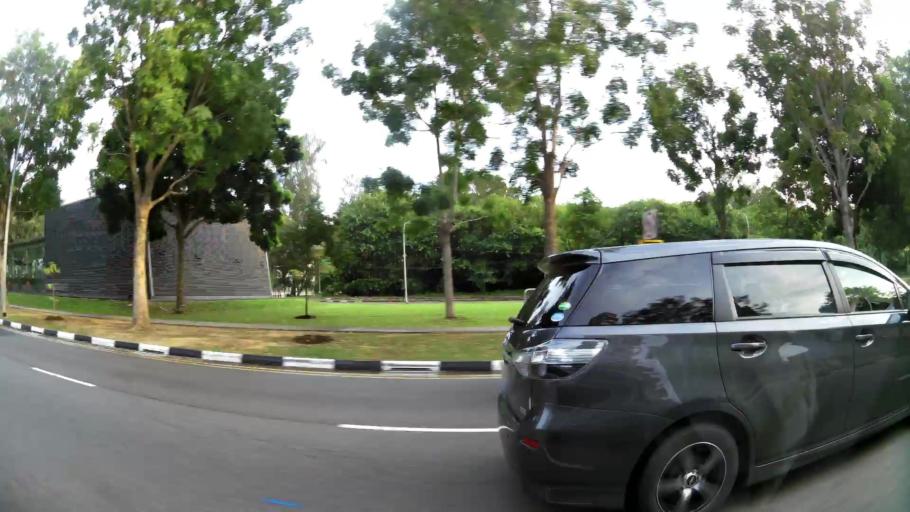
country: SG
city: Singapore
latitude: 1.2996
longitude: 103.8636
